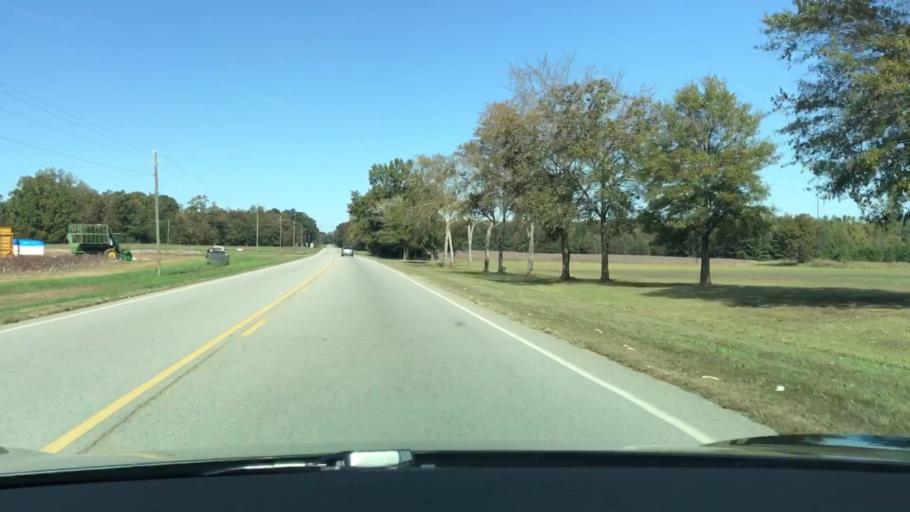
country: US
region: Georgia
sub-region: Warren County
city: Firing Range
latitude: 33.4254
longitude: -82.6826
